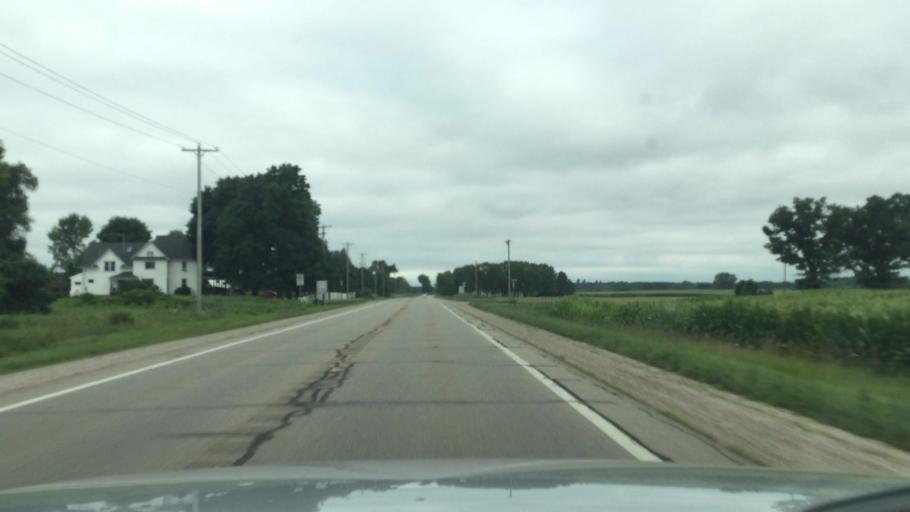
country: US
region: Michigan
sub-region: Montcalm County
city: Greenville
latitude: 43.1702
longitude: -85.1865
